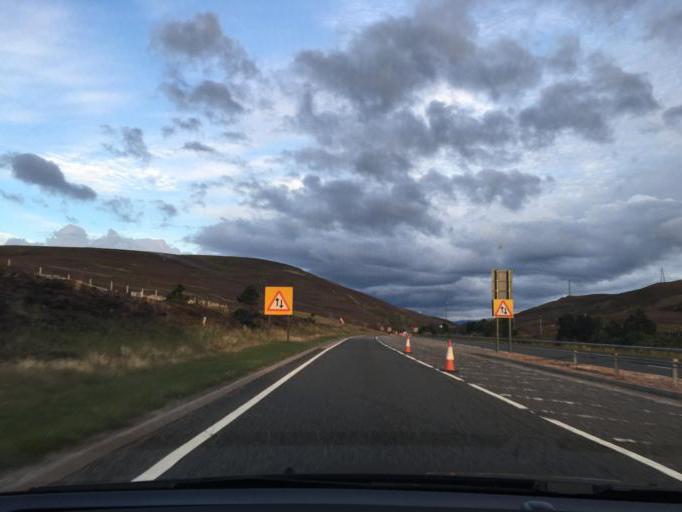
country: GB
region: Scotland
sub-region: Highland
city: Aviemore
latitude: 57.3102
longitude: -3.9434
